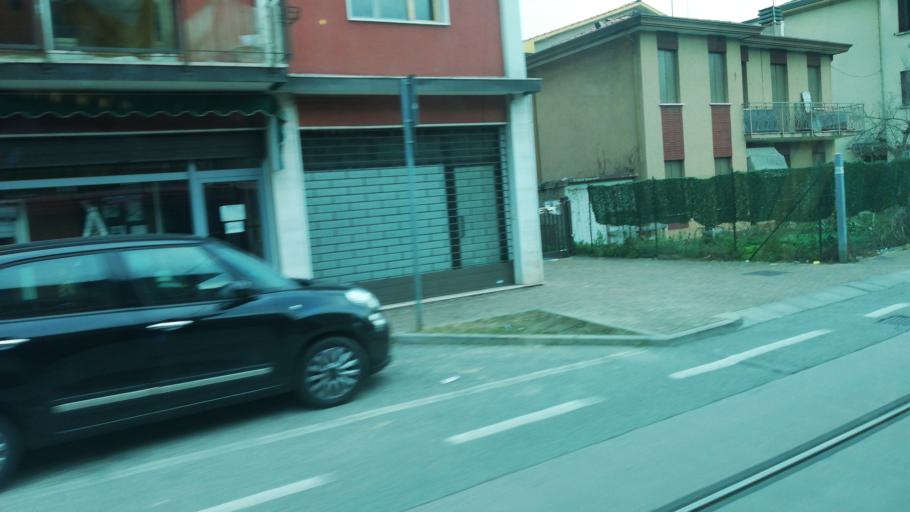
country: IT
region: Veneto
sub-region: Provincia di Venezia
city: Mestre
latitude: 45.5030
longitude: 12.2550
